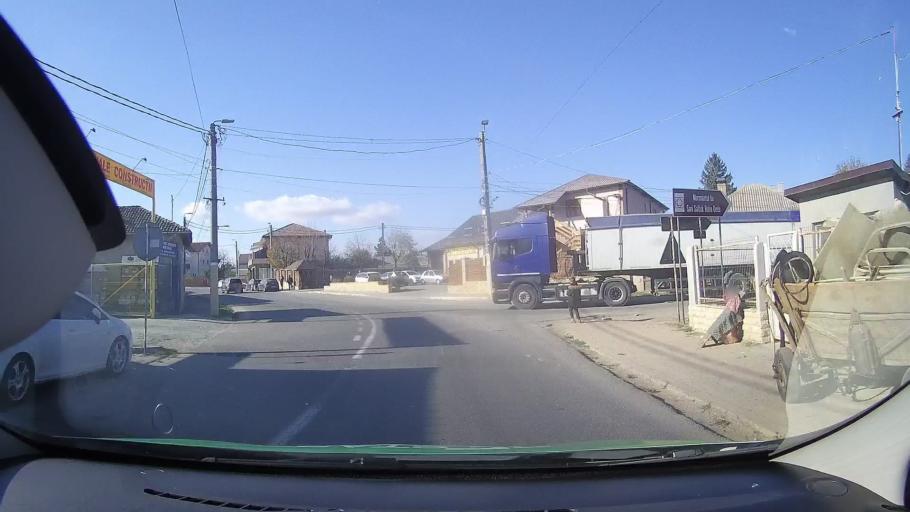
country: RO
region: Tulcea
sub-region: Oras Babadag
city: Babadag
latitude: 44.8930
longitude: 28.7186
